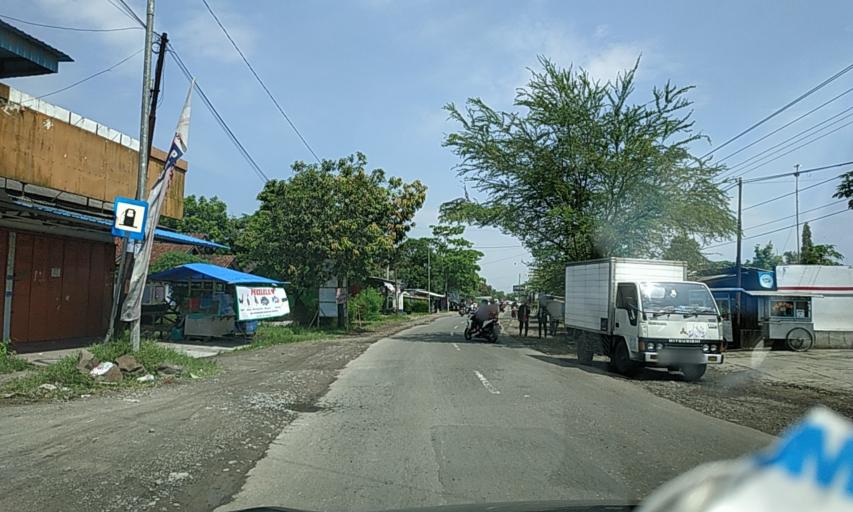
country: ID
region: Central Java
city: Tambangan
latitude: -7.4866
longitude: 108.8198
